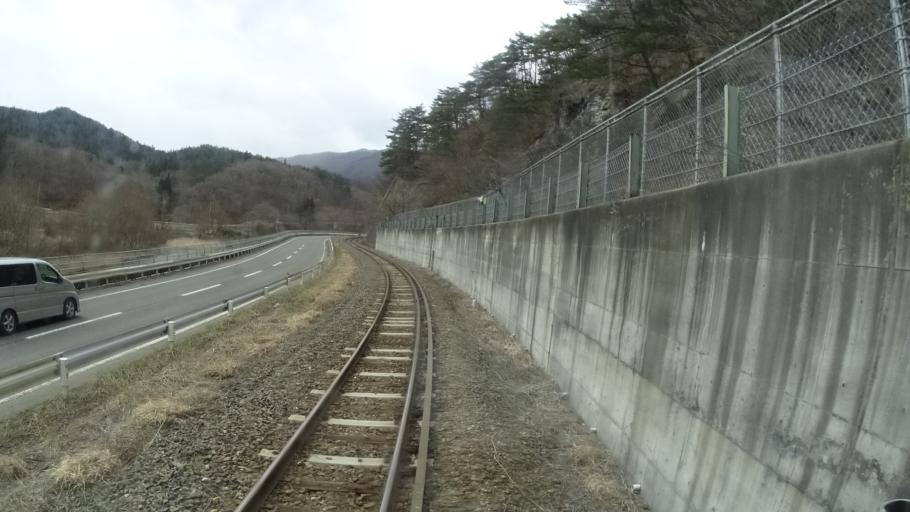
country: JP
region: Iwate
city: Tono
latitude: 39.3036
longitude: 141.3889
